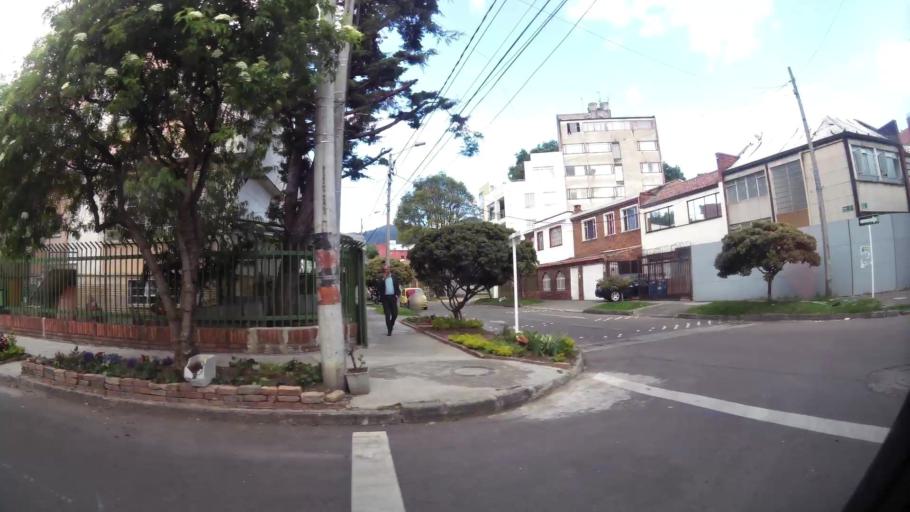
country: CO
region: Bogota D.C.
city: Bogota
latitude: 4.6463
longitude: -74.0717
